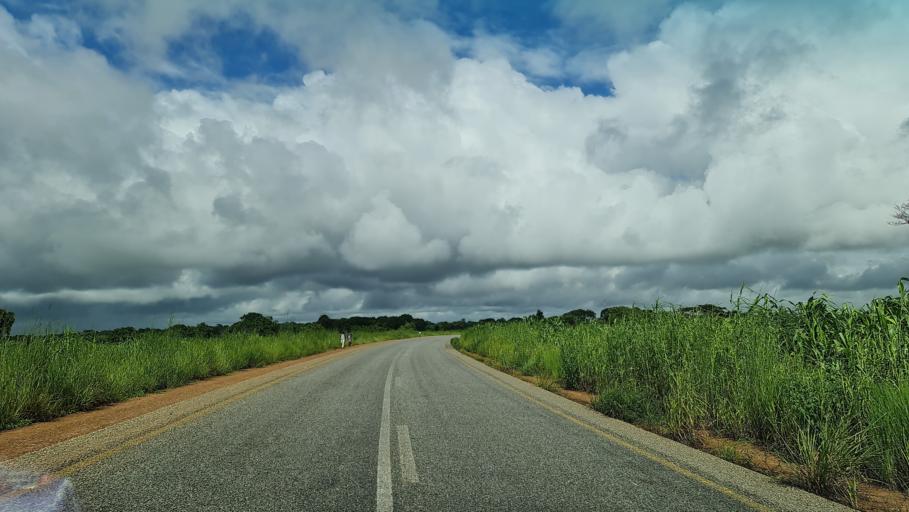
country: MZ
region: Nampula
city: Nampula
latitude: -15.0304
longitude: 38.4506
